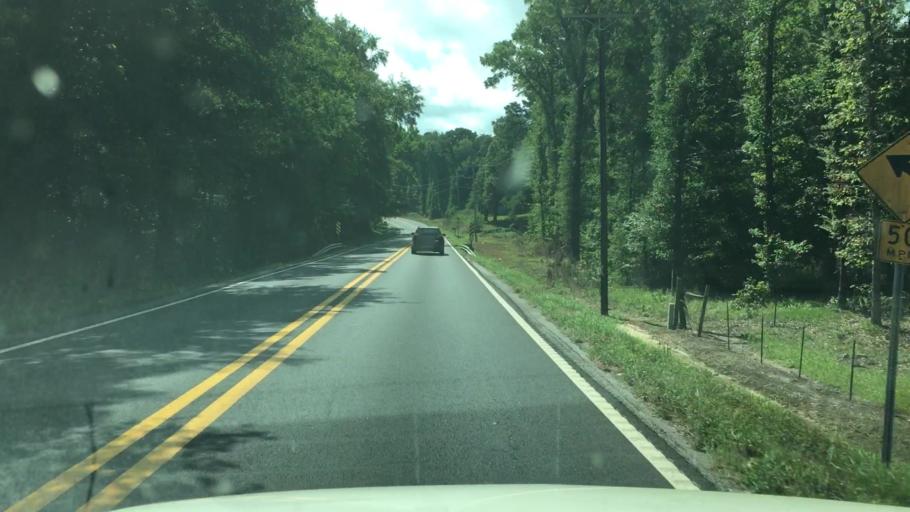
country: US
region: Arkansas
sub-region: Clark County
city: Arkadelphia
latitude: 34.2514
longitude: -93.1215
